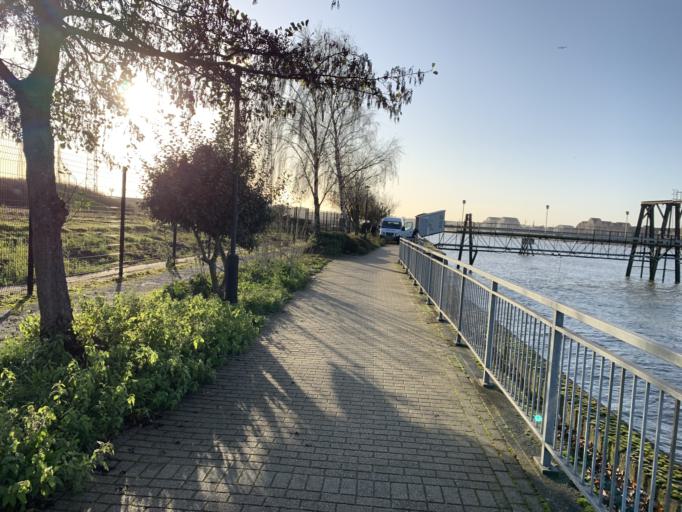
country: GB
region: England
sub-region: Greater London
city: Poplar
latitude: 51.5004
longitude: -0.0022
